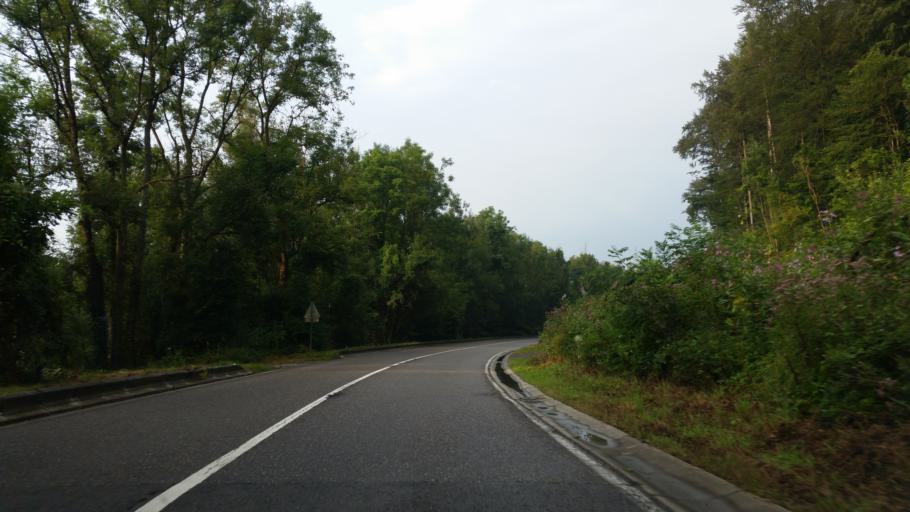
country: BE
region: Wallonia
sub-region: Province de Namur
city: Rochefort
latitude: 50.1489
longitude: 5.1972
